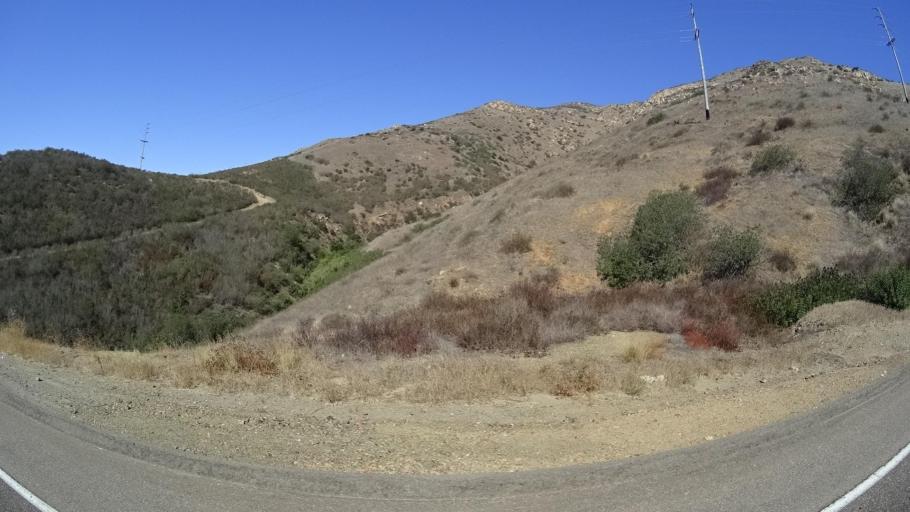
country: US
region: California
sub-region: San Diego County
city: Fairbanks Ranch
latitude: 33.0435
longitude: -117.1330
